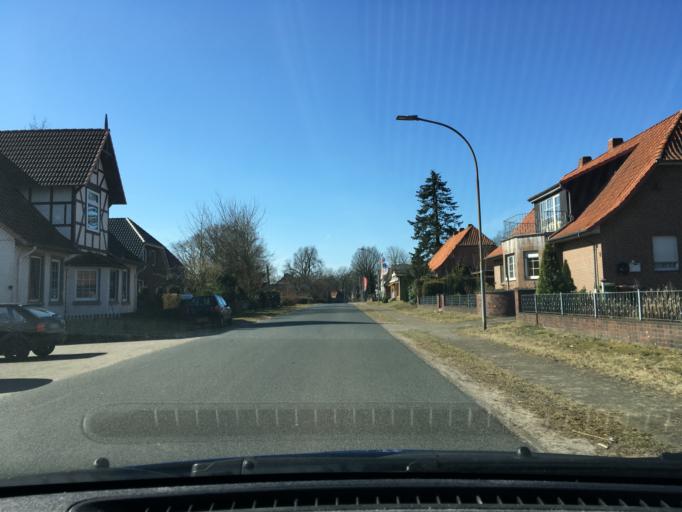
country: DE
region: Lower Saxony
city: Neuenkirchen
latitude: 53.0684
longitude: 9.6721
